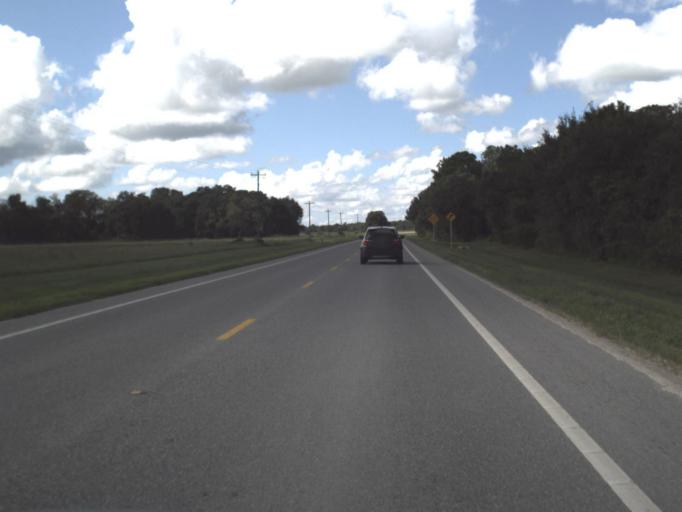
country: US
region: Florida
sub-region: DeSoto County
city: Arcadia
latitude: 27.3252
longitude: -82.1275
